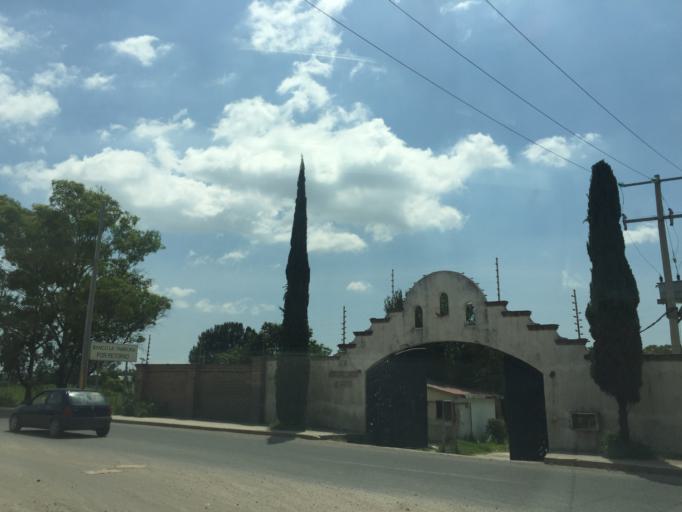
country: MX
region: Guanajuato
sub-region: Leon
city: Fraccionamiento Paseo de las Torres
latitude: 21.1898
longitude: -101.7472
